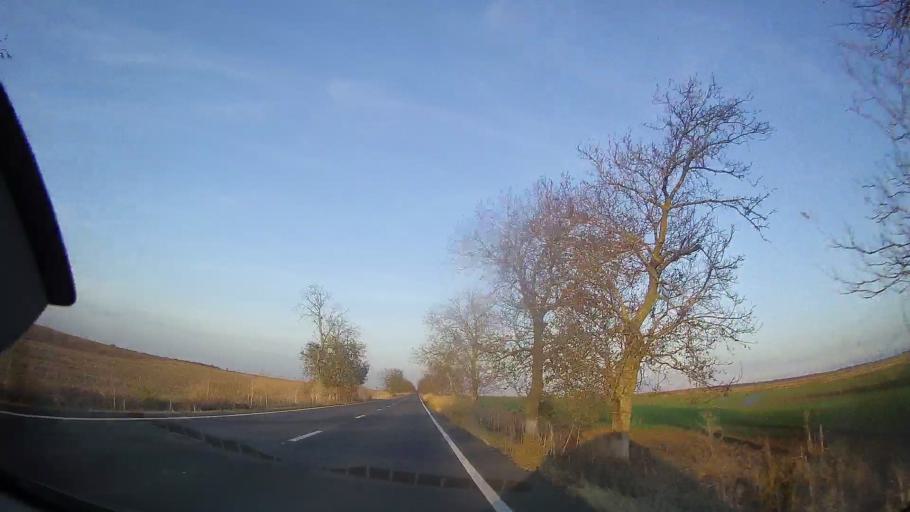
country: RO
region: Constanta
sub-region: Comuna Amzacea
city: Amzacea
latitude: 43.9457
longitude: 28.3766
